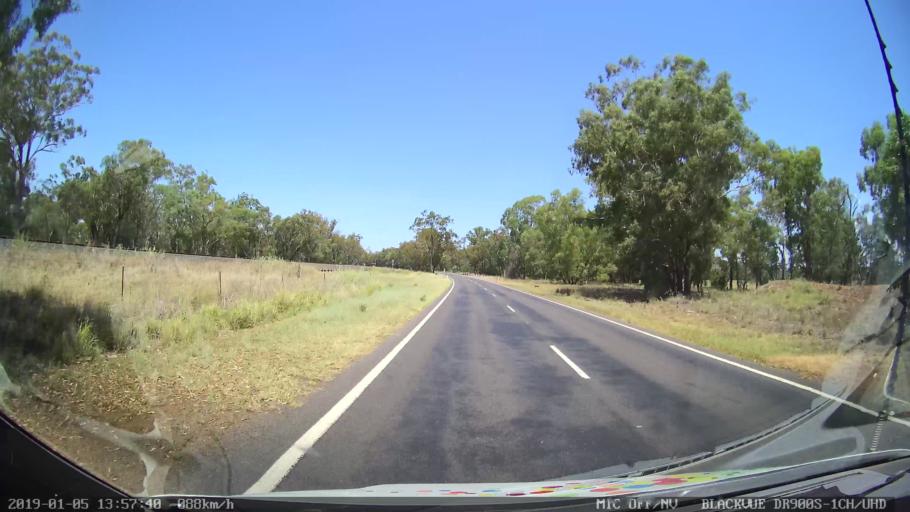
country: AU
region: New South Wales
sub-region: Gunnedah
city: Gunnedah
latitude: -31.1303
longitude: 150.2760
